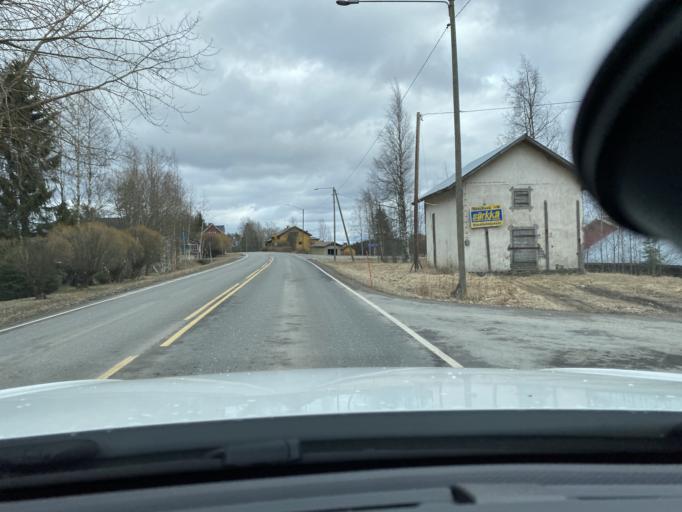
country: FI
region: Pirkanmaa
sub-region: Lounais-Pirkanmaa
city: Punkalaidun
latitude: 61.1006
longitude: 23.2031
